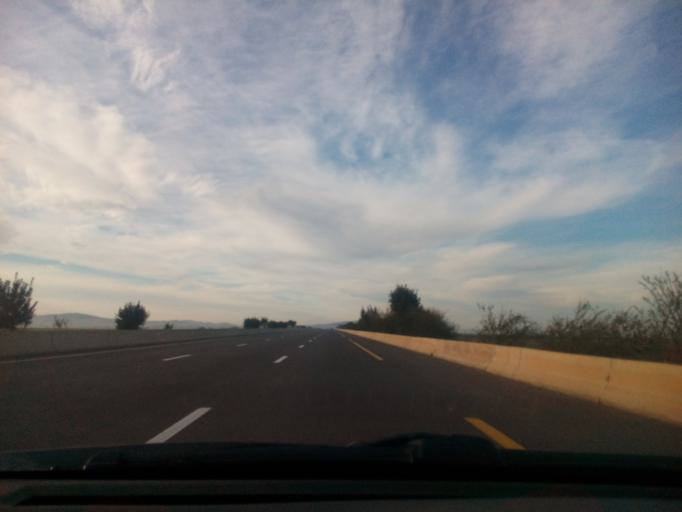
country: DZ
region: Mostaganem
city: Mostaganem
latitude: 35.6749
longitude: 0.1484
